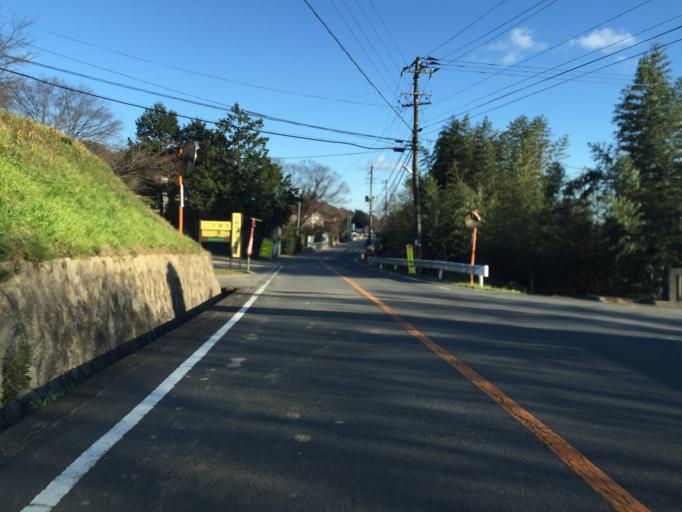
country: JP
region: Fukushima
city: Iwaki
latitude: 37.1421
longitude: 140.8397
